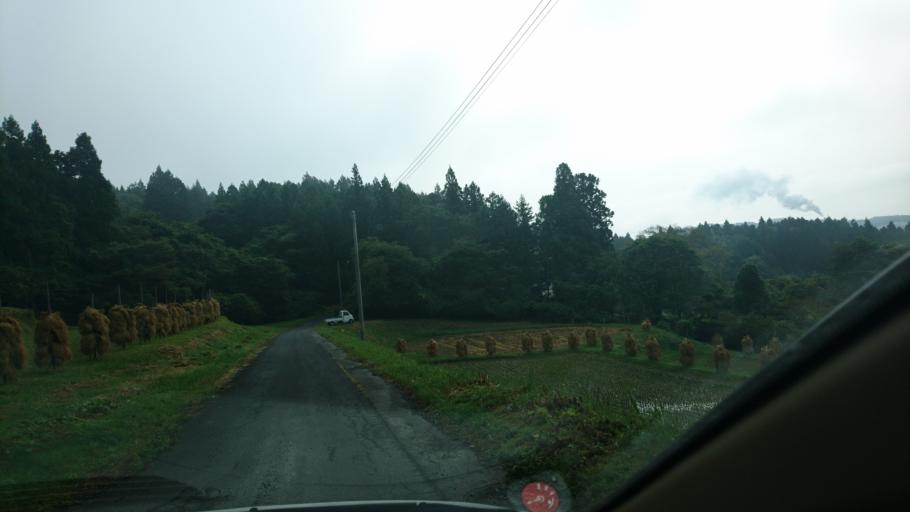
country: JP
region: Iwate
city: Ichinoseki
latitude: 38.9589
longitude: 141.1851
